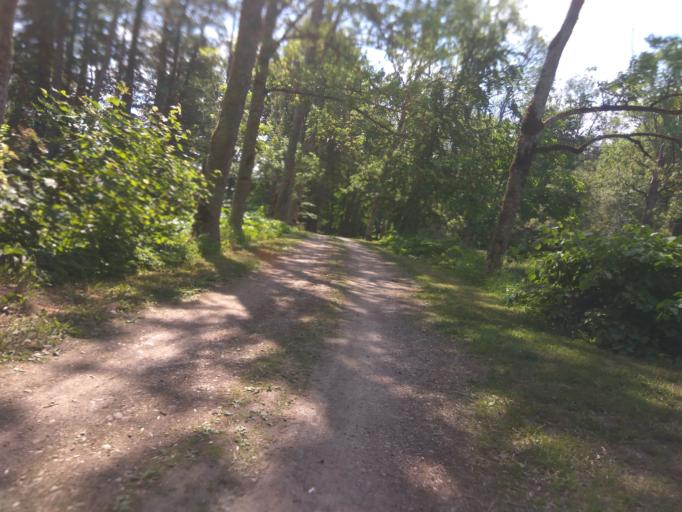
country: LV
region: Kuldigas Rajons
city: Kuldiga
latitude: 56.9205
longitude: 21.9705
